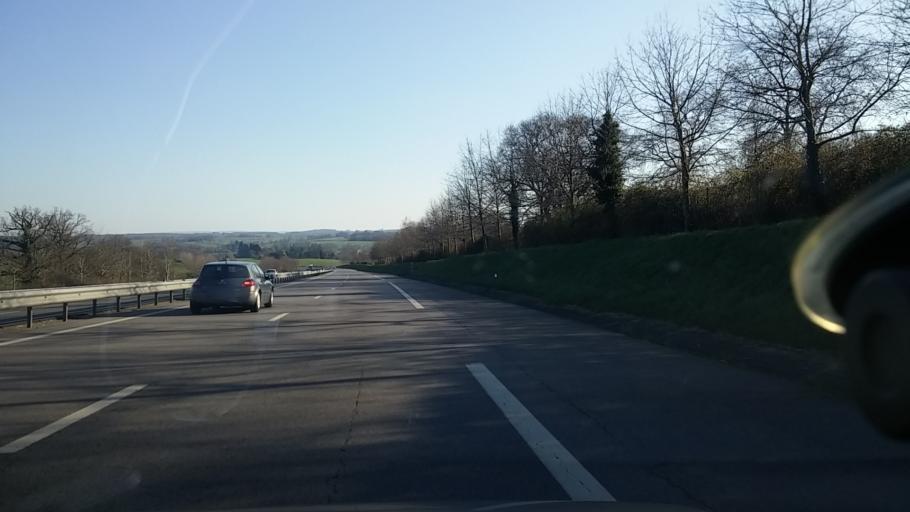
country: FR
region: Limousin
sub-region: Departement de la Haute-Vienne
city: Saint-Sulpice-les-Feuilles
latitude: 46.3038
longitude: 1.4155
